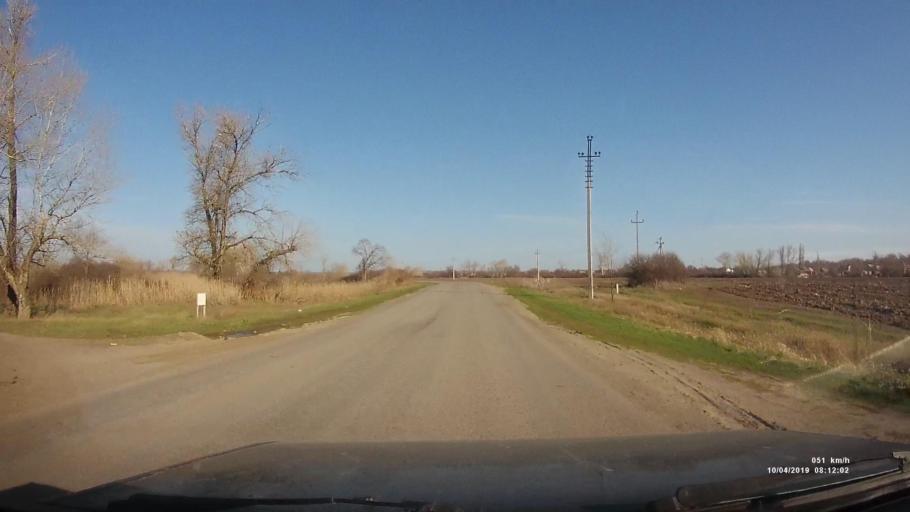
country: RU
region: Rostov
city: Staraya Stanitsa
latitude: 48.3604
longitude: 40.2614
